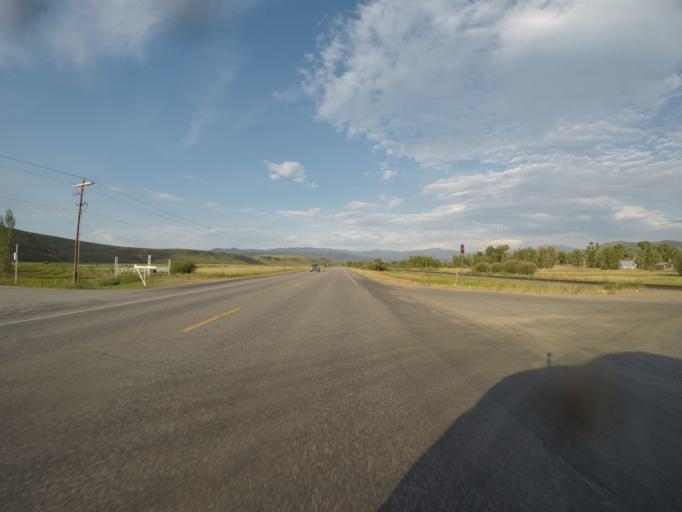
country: US
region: Colorado
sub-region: Routt County
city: Steamboat Springs
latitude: 40.4930
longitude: -106.9516
